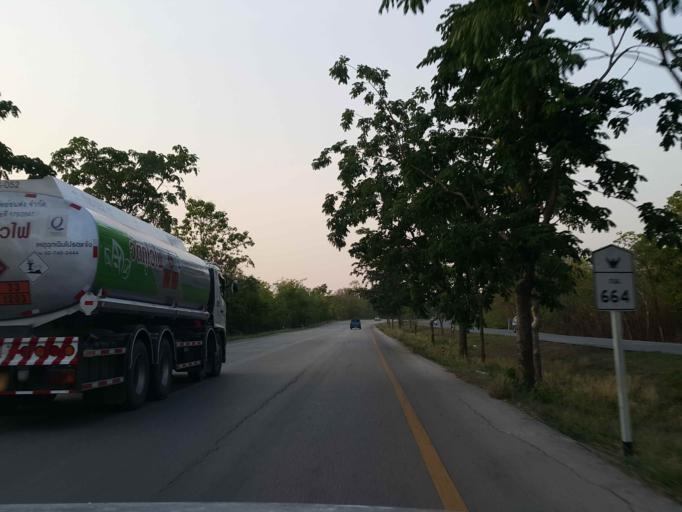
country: TH
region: Lampang
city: Sop Prap
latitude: 17.9783
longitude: 99.3557
